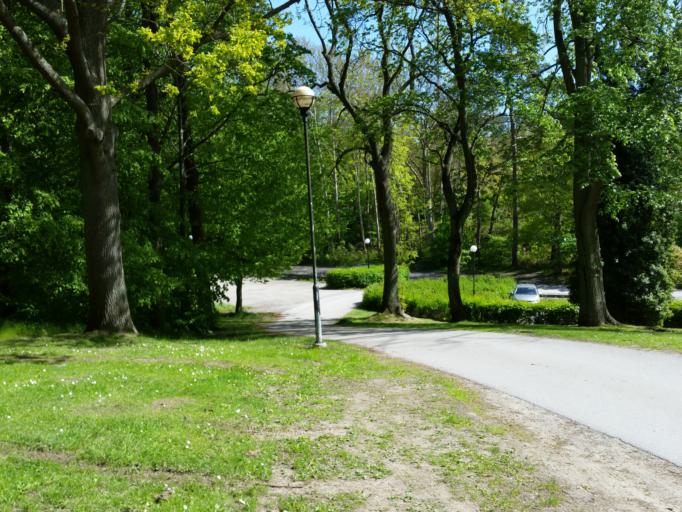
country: SE
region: Blekinge
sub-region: Karlshamns Kommun
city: Karlshamn
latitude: 56.1720
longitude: 14.8698
